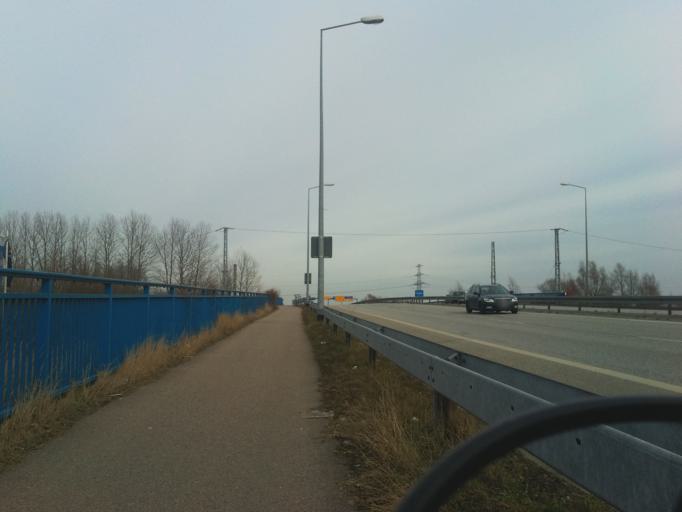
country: DE
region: Mecklenburg-Vorpommern
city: Dierkow-Neu
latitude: 54.1036
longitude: 12.1830
